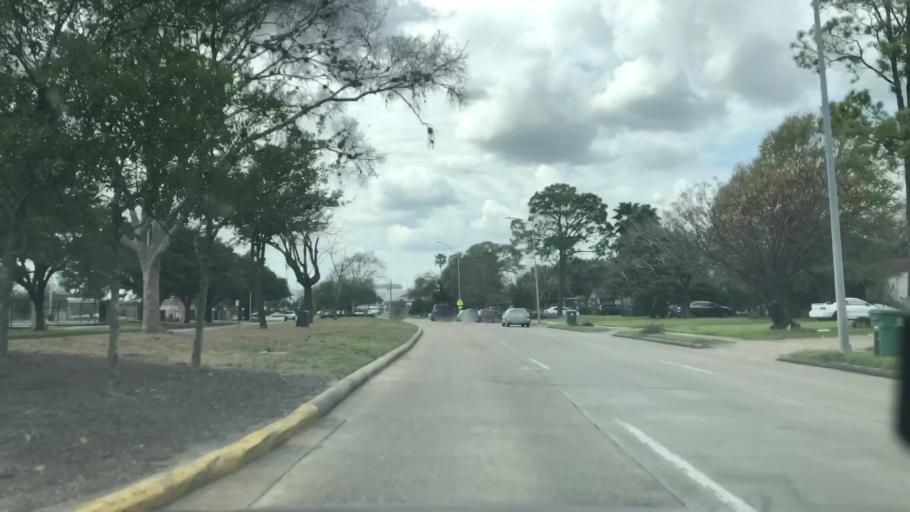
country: US
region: Texas
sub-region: Harris County
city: Bellaire
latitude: 29.6920
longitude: -95.5071
